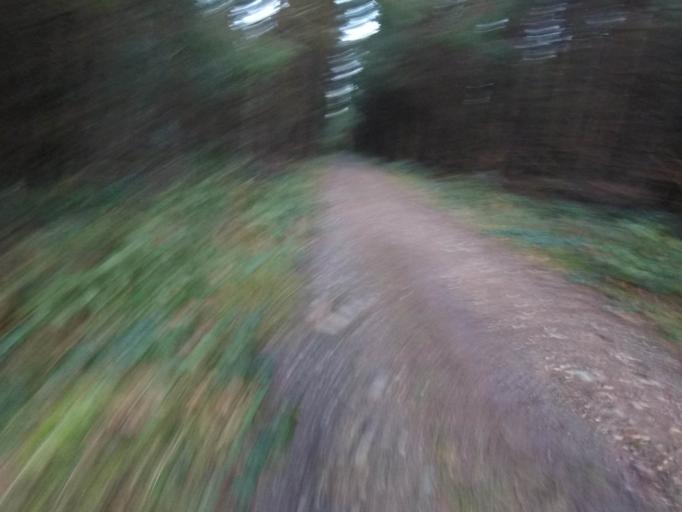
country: IE
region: Munster
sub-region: Waterford
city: Portlaw
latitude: 52.3124
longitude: -7.3455
